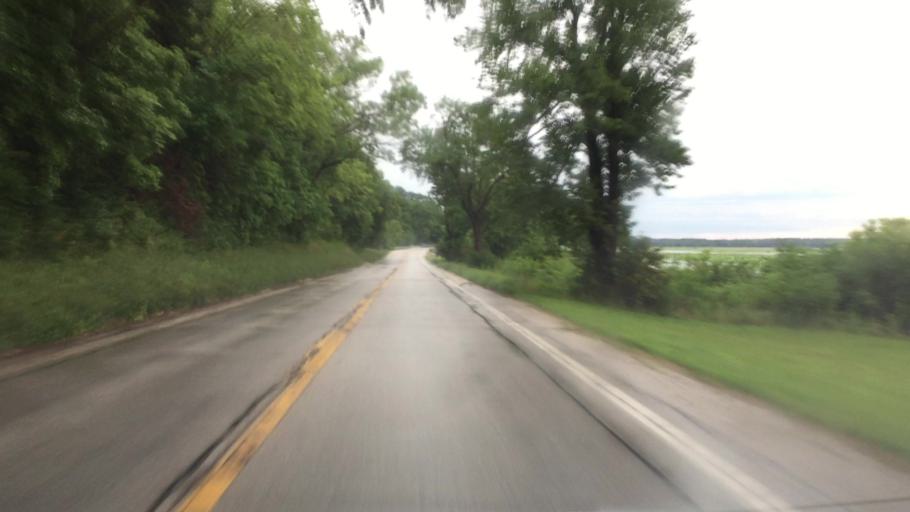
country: US
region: Iowa
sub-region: Lee County
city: Keokuk
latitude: 40.4314
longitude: -91.3685
